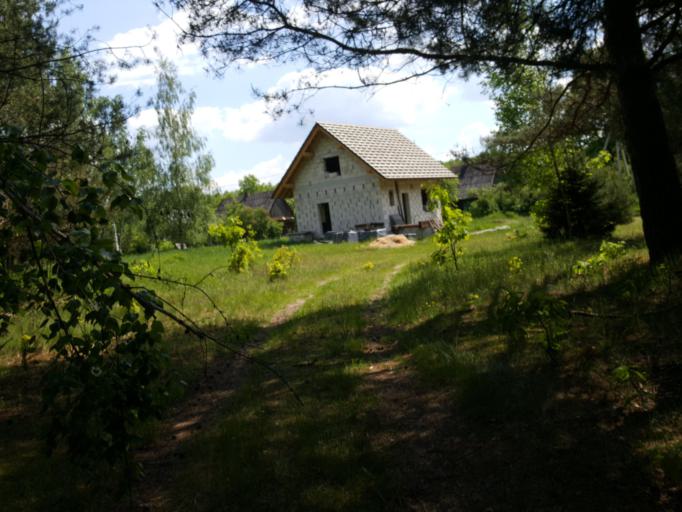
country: PL
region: Podlasie
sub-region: Powiat hajnowski
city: Hajnowka
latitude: 52.5868
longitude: 23.6080
